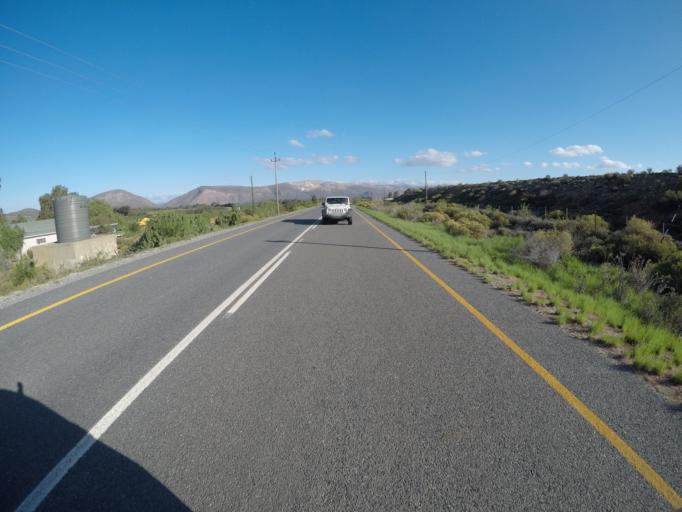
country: ZA
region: Western Cape
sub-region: Cape Winelands District Municipality
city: Ashton
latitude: -33.7948
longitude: 19.7806
